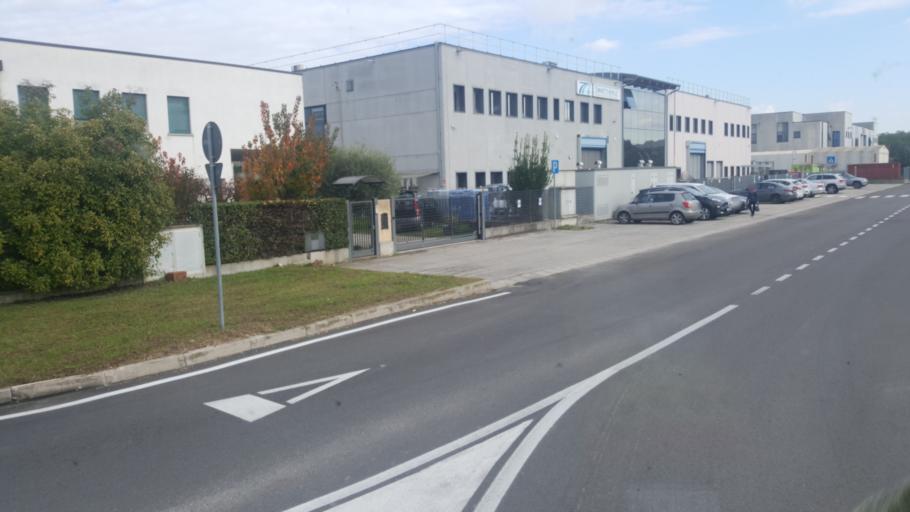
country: IT
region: Veneto
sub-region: Provincia di Vicenza
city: Ponte di Castegnero
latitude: 45.4426
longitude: 11.5970
